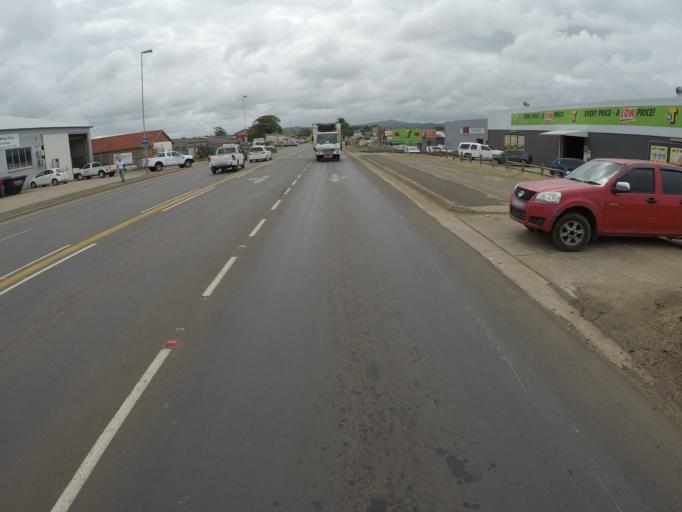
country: ZA
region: KwaZulu-Natal
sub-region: uThungulu District Municipality
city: Empangeni
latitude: -28.7779
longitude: 31.8974
